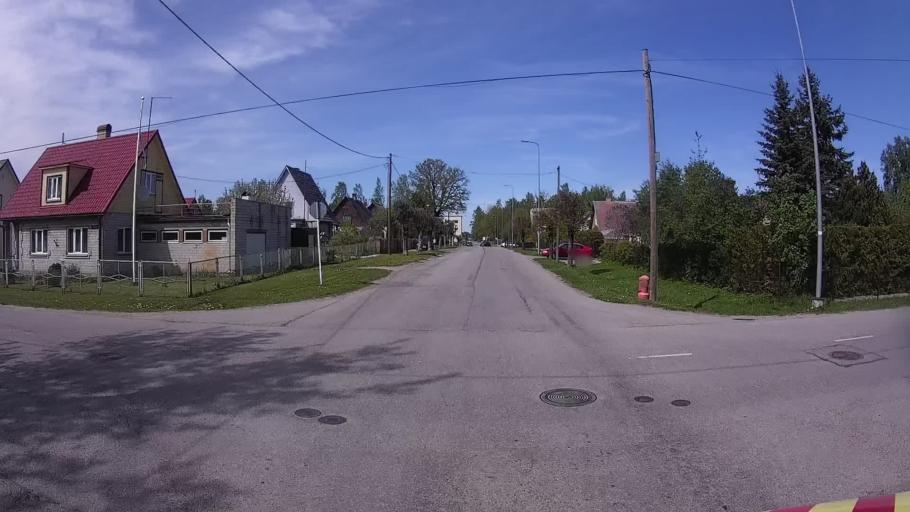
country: EE
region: Valgamaa
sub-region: Valga linn
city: Valga
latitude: 57.7800
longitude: 26.0629
